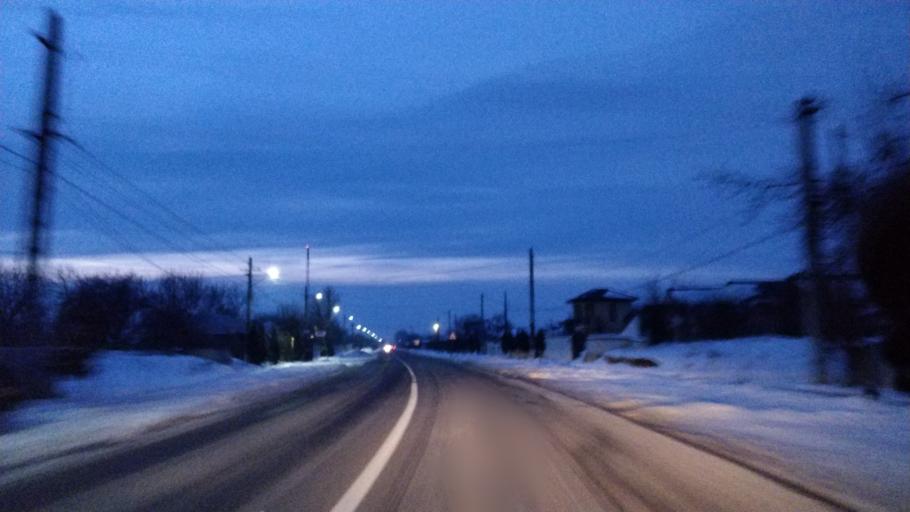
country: RO
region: Vrancea
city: Vulturu de Sus
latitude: 45.6346
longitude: 27.3819
